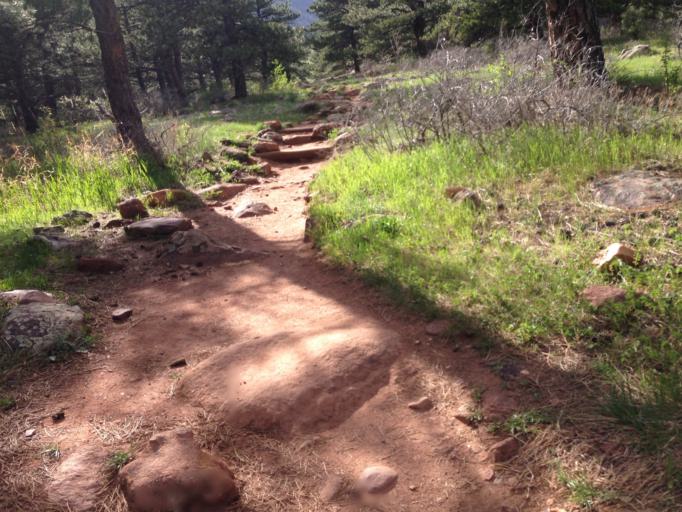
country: US
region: Colorado
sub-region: Boulder County
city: Boulder
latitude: 39.9416
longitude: -105.2698
